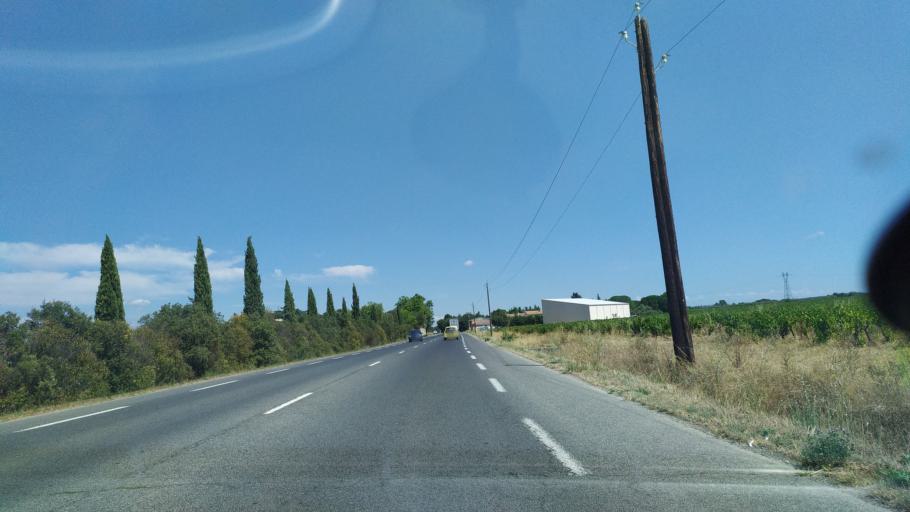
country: FR
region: Languedoc-Roussillon
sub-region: Departement du Gard
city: Aubord
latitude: 43.7652
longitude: 4.3196
